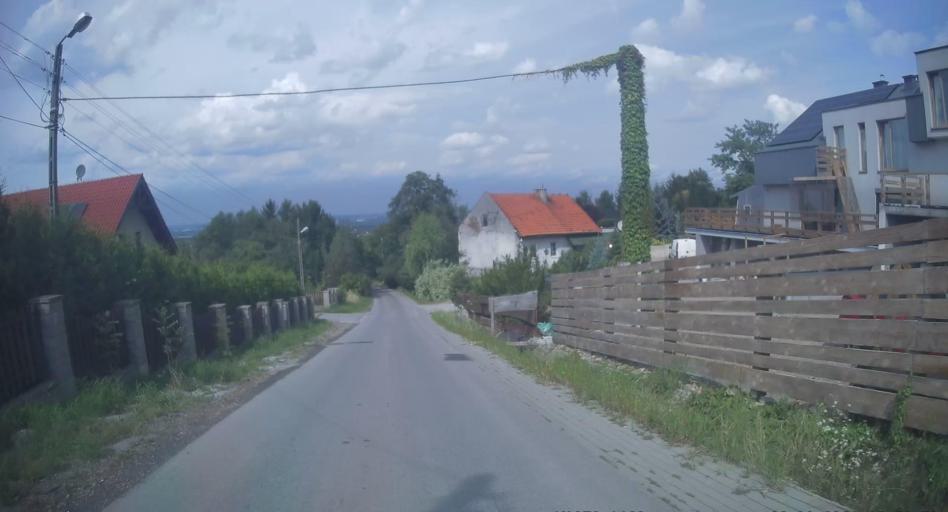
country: PL
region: Lesser Poland Voivodeship
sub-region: Powiat wielicki
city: Wieliczka
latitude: 49.9748
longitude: 20.0548
